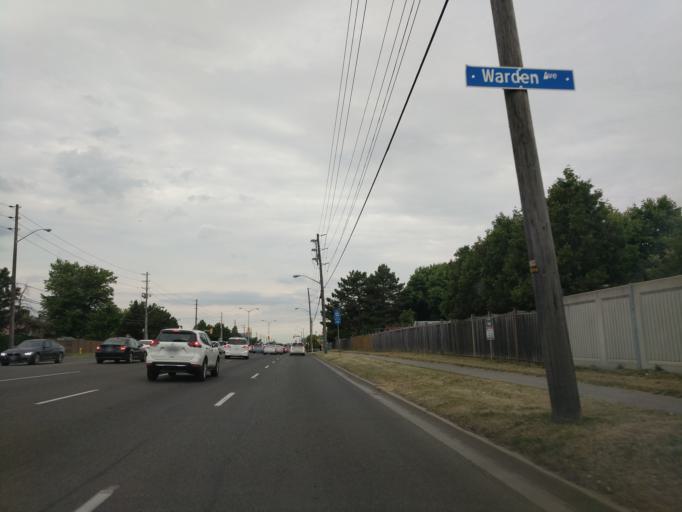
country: CA
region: Ontario
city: Markham
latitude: 43.8202
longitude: -79.3226
